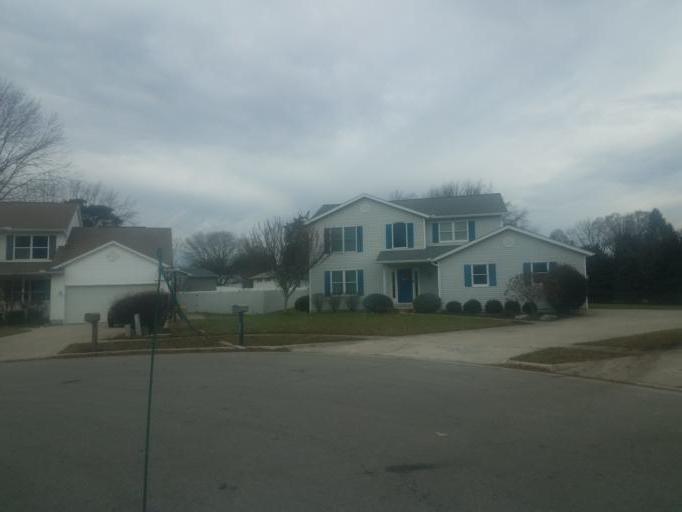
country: US
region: Ohio
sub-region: Marion County
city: Marion
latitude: 40.5693
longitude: -83.0848
